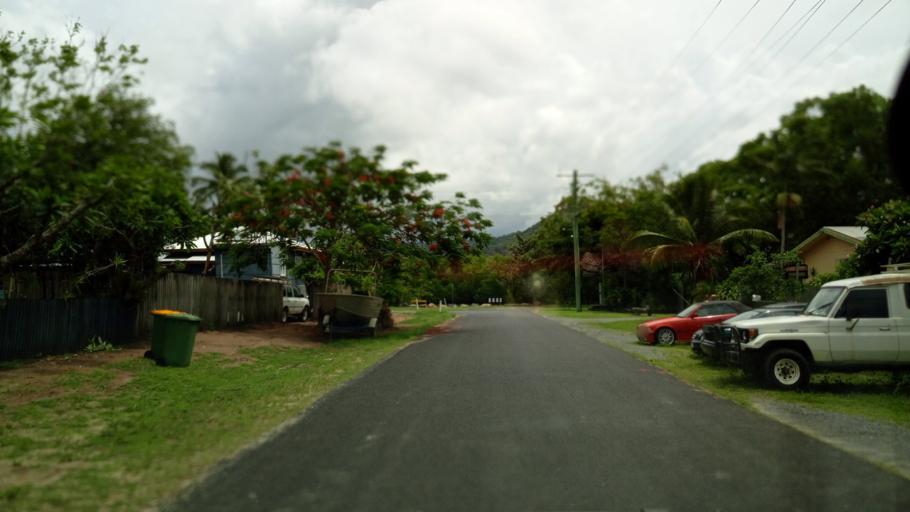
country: AU
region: Queensland
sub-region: Cairns
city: Redlynch
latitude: -16.8592
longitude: 145.7450
